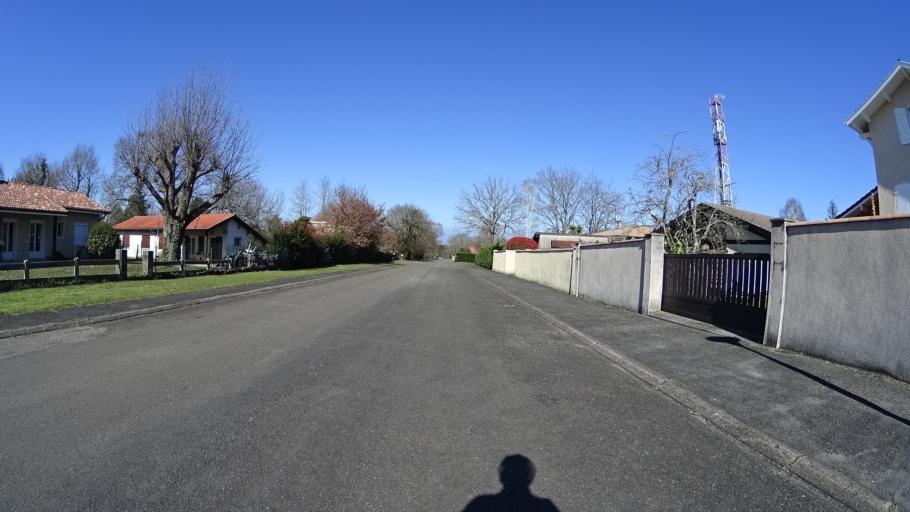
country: FR
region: Aquitaine
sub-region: Departement des Landes
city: Saint-Paul-les-Dax
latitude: 43.7329
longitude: -1.0851
